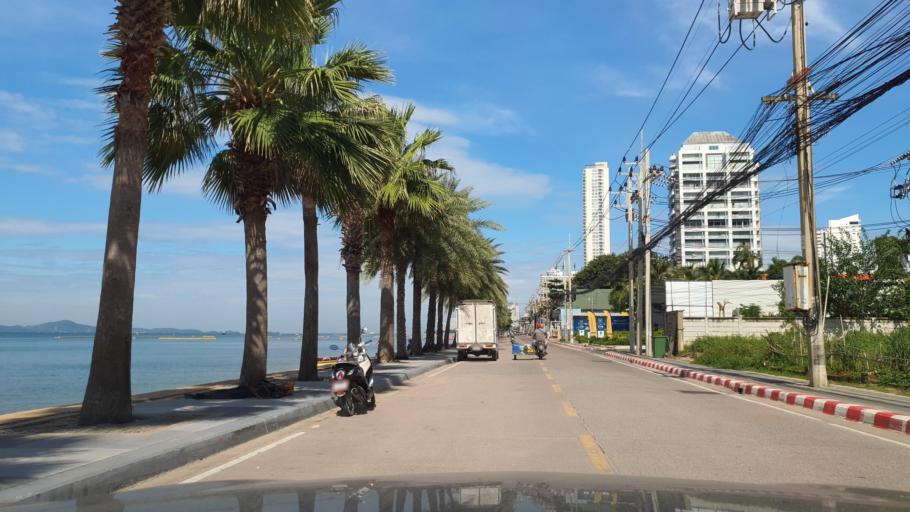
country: TH
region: Chon Buri
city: Phatthaya
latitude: 12.8692
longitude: 100.8906
